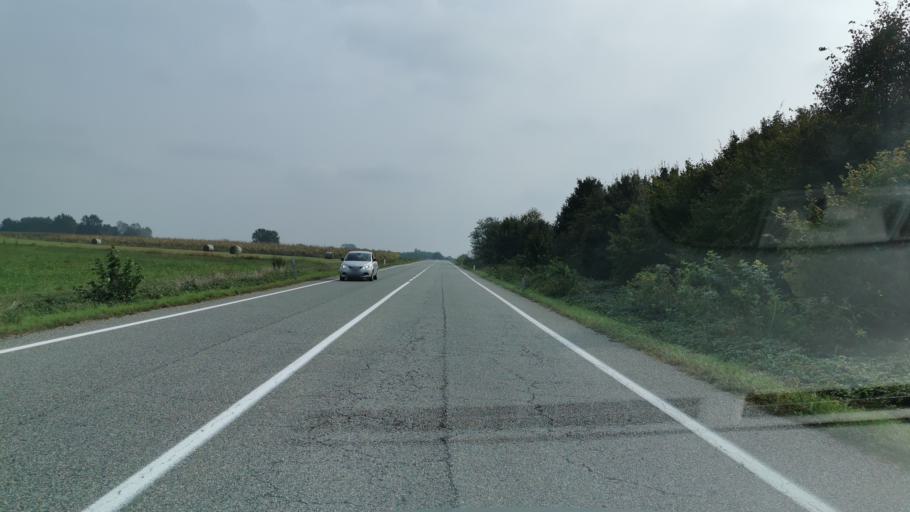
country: IT
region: Piedmont
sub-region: Provincia di Torino
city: Montanaro
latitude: 45.2310
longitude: 7.8716
